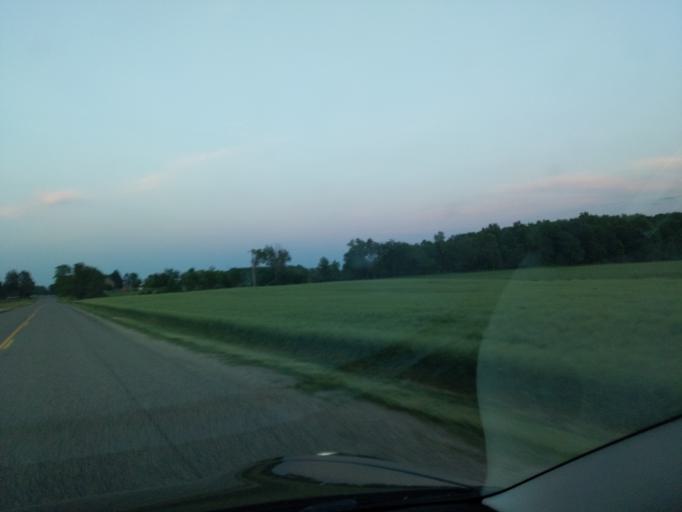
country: US
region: Michigan
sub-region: Eaton County
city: Bellevue
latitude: 42.5385
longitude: -84.9916
